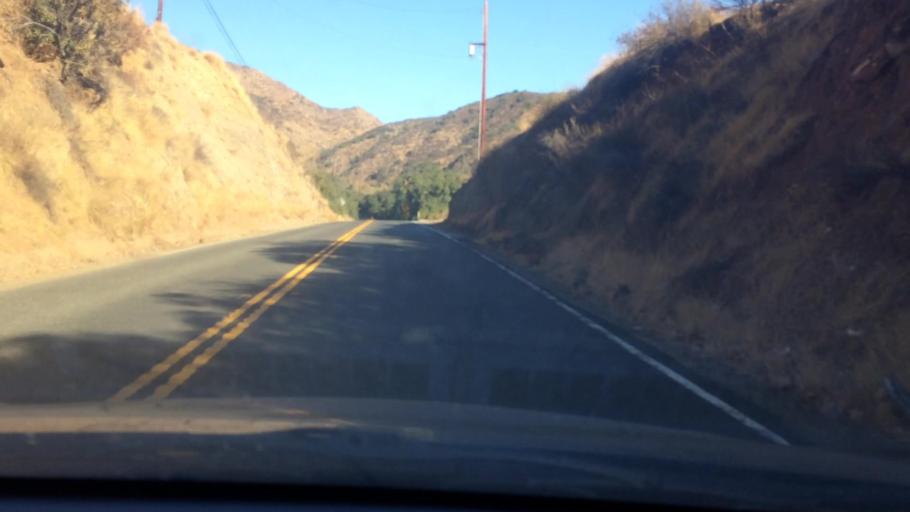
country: US
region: California
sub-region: Orange County
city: Coto De Caza
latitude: 33.5870
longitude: -117.5204
